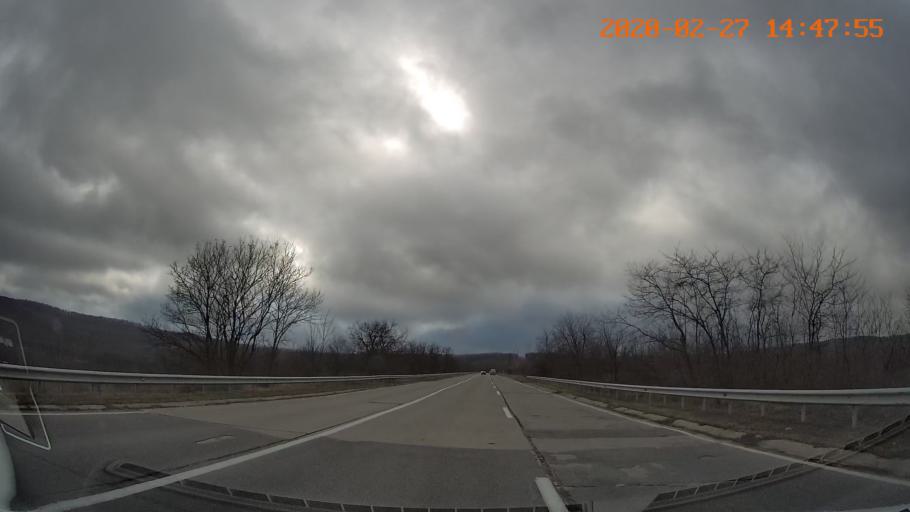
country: MD
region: Straseni
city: Straseni
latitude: 47.2159
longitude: 28.6246
